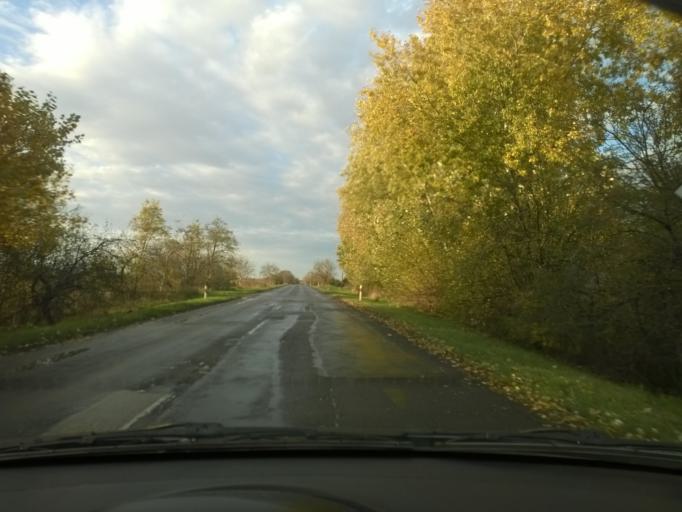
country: HU
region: Bacs-Kiskun
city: Kalocsa
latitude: 46.5446
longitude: 18.9846
